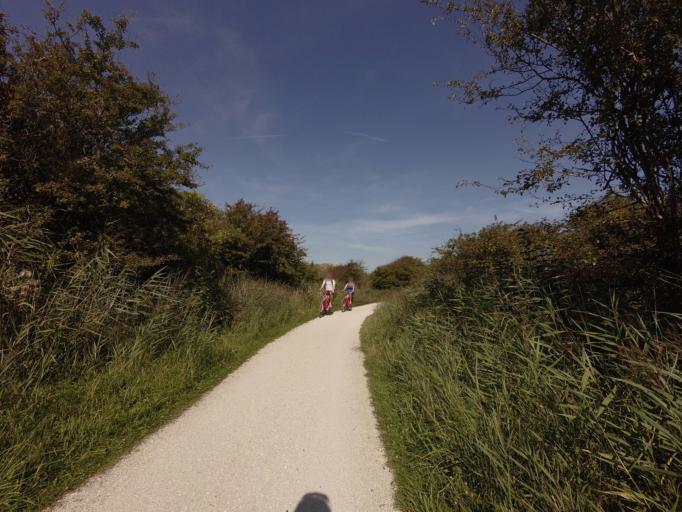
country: NL
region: Friesland
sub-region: Gemeente Schiermonnikoog
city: Schiermonnikoog
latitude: 53.4823
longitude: 6.1454
